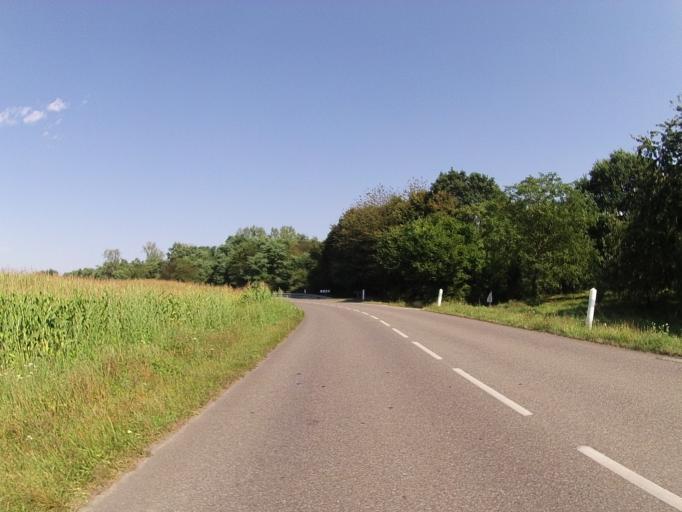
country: FR
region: Alsace
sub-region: Departement du Bas-Rhin
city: Seltz
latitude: 48.9162
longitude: 8.1256
